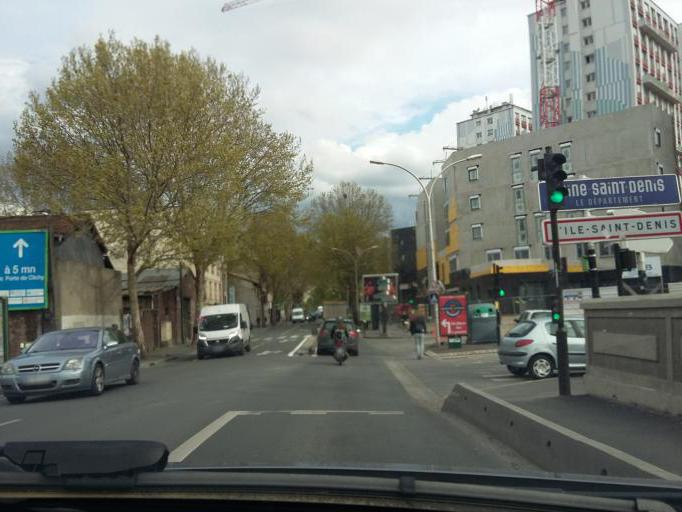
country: FR
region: Ile-de-France
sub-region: Paris
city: Saint-Ouen
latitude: 48.9205
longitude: 2.3261
